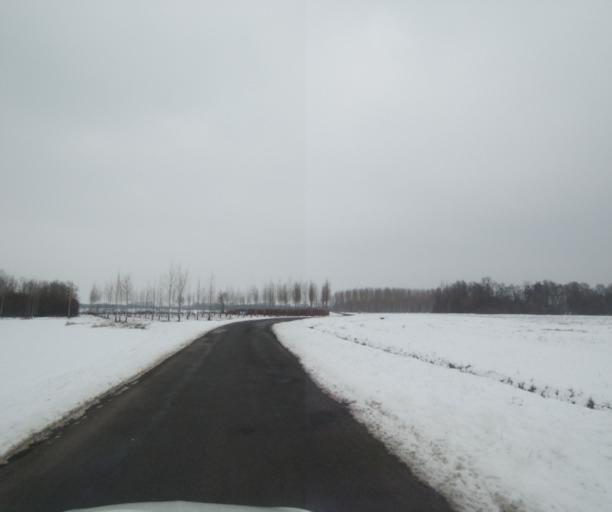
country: FR
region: Champagne-Ardenne
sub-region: Departement de la Haute-Marne
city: Saint-Dizier
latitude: 48.5692
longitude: 4.8908
